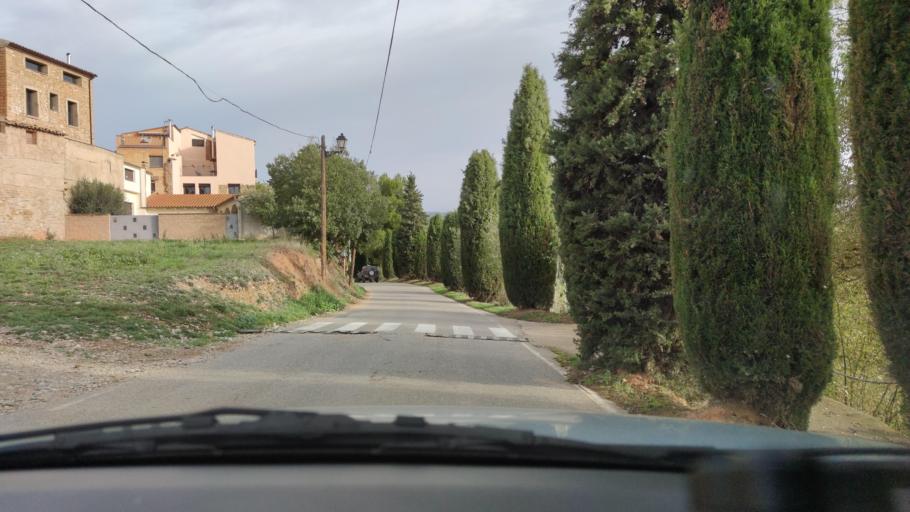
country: ES
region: Catalonia
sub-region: Provincia de Lleida
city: Artesa de Segre
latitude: 41.9171
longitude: 1.0155
